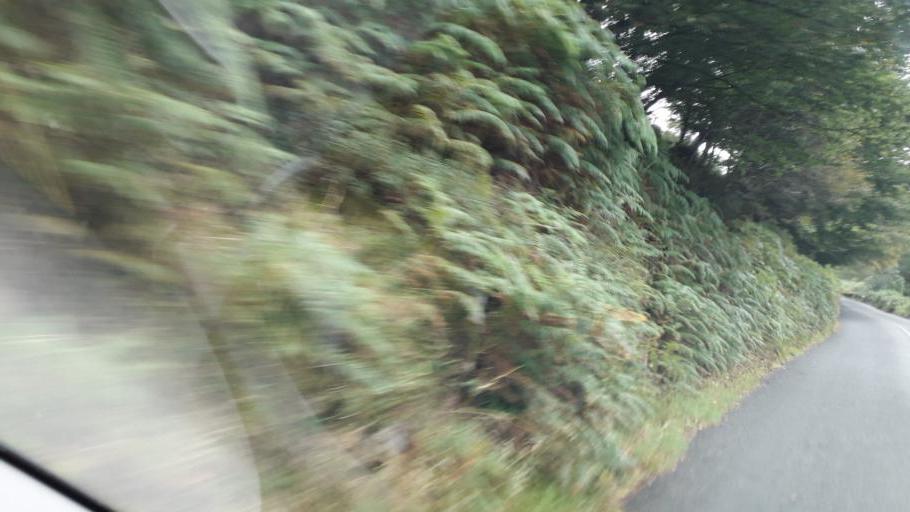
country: IE
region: Leinster
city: Ballinteer
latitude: 53.2402
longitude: -6.2890
